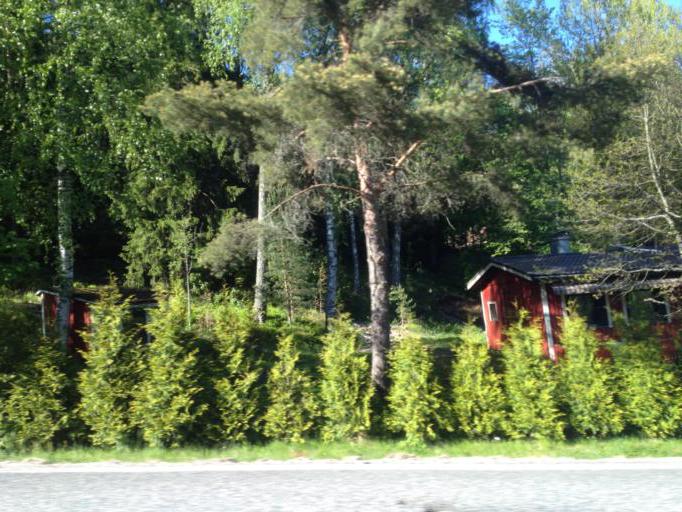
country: FI
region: Uusimaa
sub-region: Helsinki
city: Espoo
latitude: 60.2883
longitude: 24.5721
